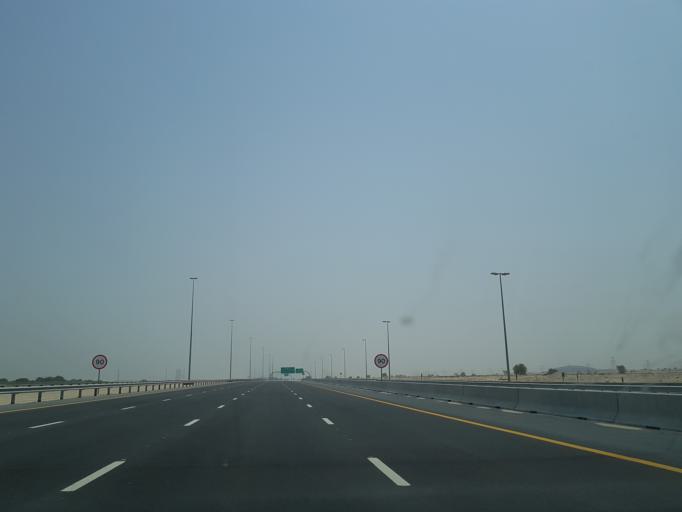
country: AE
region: Dubai
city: Dubai
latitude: 25.0506
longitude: 55.2882
